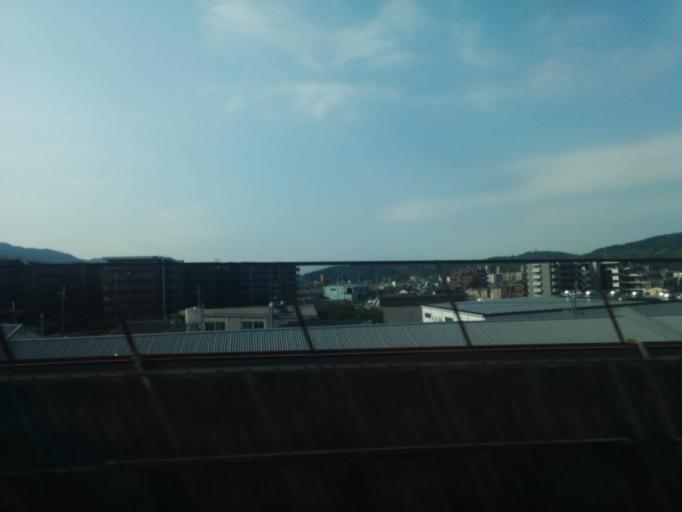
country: JP
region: Shiga Prefecture
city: Otsu-shi
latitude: 34.9810
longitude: 135.8106
